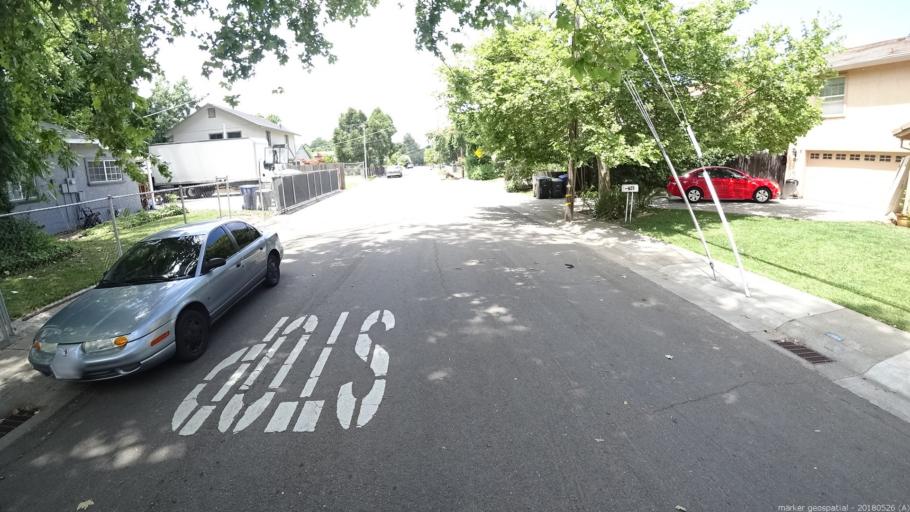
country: US
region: California
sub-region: Sacramento County
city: Sacramento
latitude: 38.6092
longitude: -121.4842
